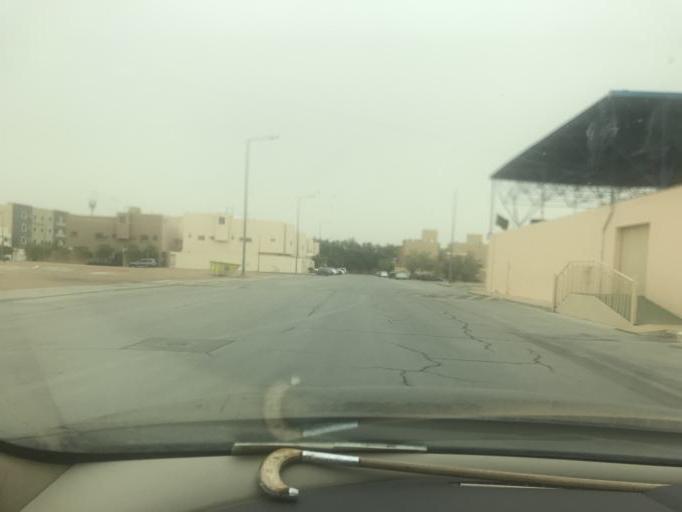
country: SA
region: Ar Riyad
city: Riyadh
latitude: 24.7287
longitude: 46.7898
